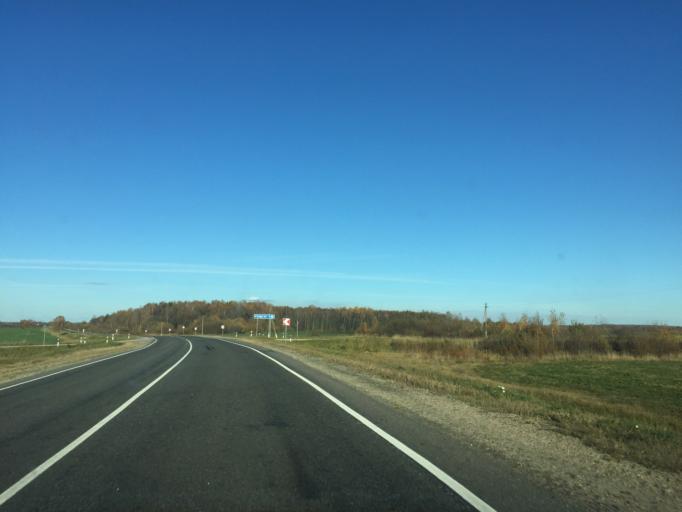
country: BY
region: Vitebsk
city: Dzisna
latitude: 55.3151
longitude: 28.2709
